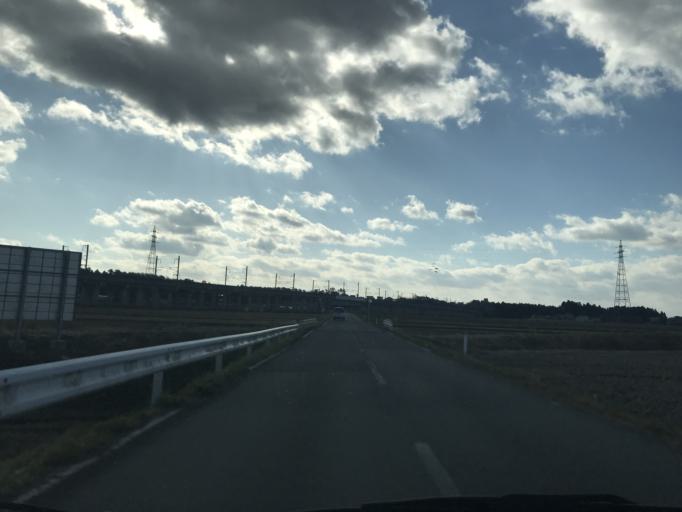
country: JP
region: Iwate
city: Ichinoseki
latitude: 38.7429
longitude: 141.0664
